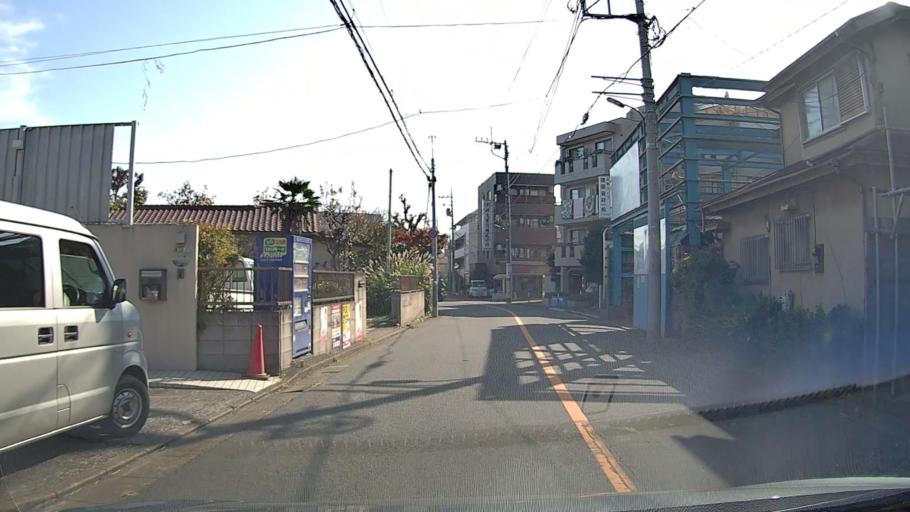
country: JP
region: Saitama
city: Wako
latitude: 35.7480
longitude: 139.6265
